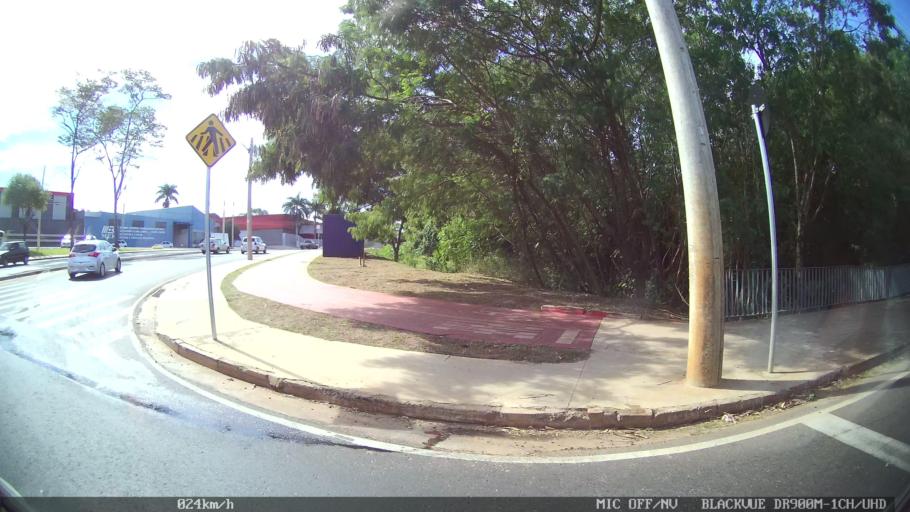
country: BR
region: Sao Paulo
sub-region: Sao Jose Do Rio Preto
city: Sao Jose do Rio Preto
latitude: -20.8414
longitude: -49.3515
